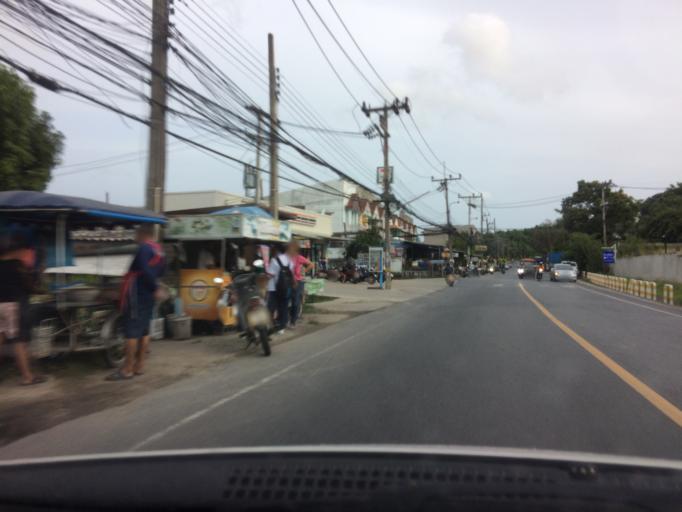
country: TH
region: Phuket
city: Ban Ratsada
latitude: 7.9004
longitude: 98.4110
